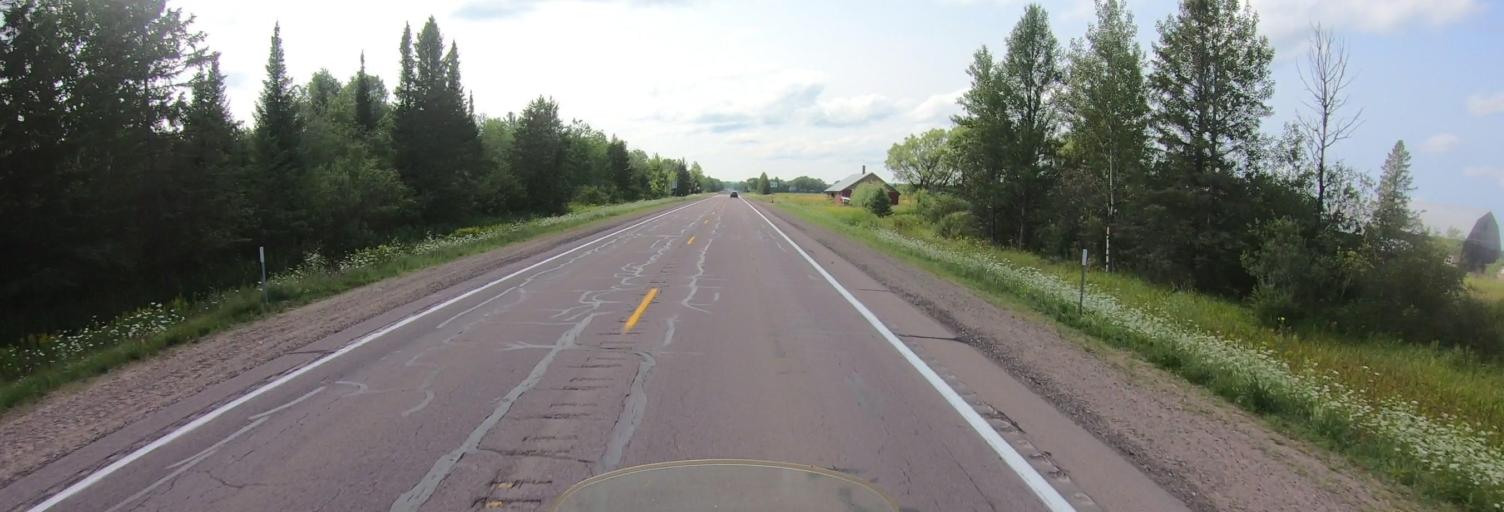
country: US
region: Michigan
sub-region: Ontonagon County
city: Ontonagon
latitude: 46.5660
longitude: -89.4446
